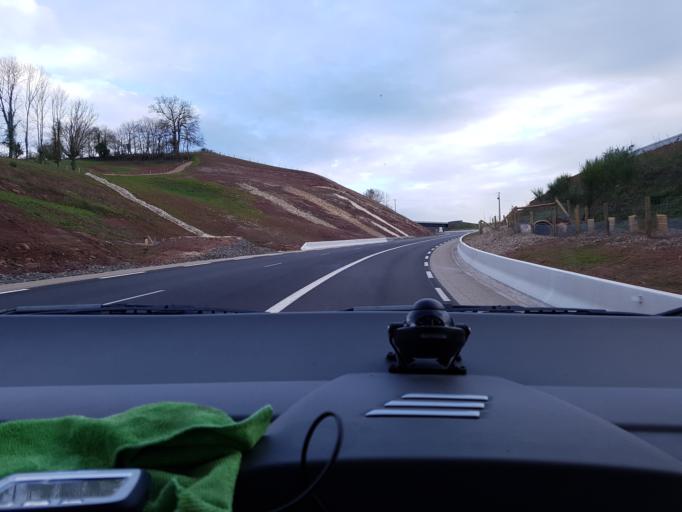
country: FR
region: Midi-Pyrenees
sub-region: Departement de l'Aveyron
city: Espalion
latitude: 44.5155
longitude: 2.7333
